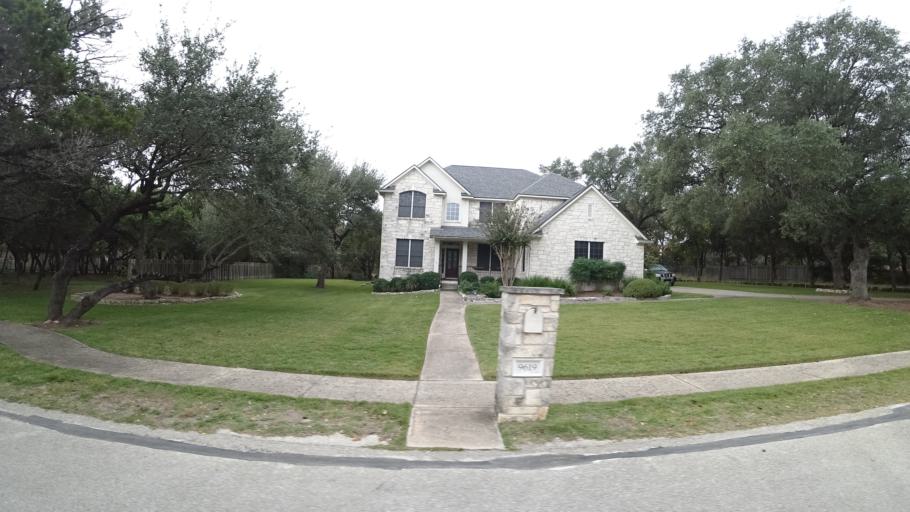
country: US
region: Texas
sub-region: Travis County
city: Barton Creek
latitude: 30.2573
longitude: -97.9083
